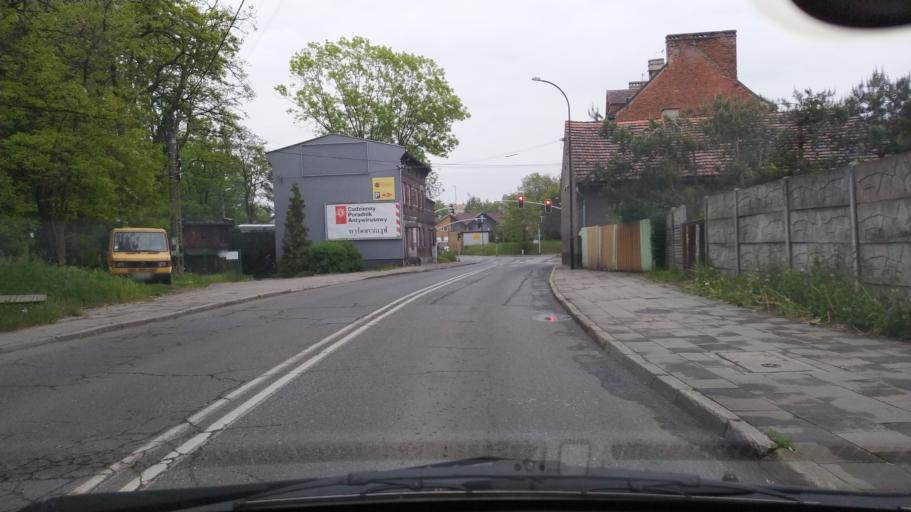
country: PL
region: Silesian Voivodeship
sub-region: Powiat gliwicki
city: Przyszowice
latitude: 50.2870
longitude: 18.7240
